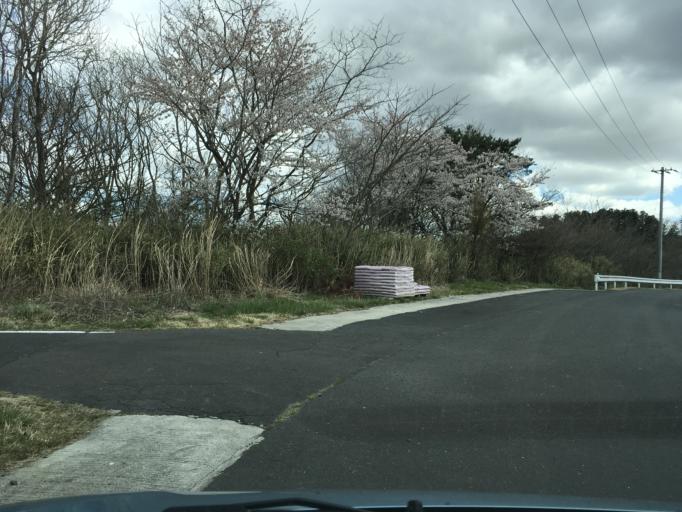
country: JP
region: Miyagi
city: Wakuya
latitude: 38.6820
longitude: 141.1230
